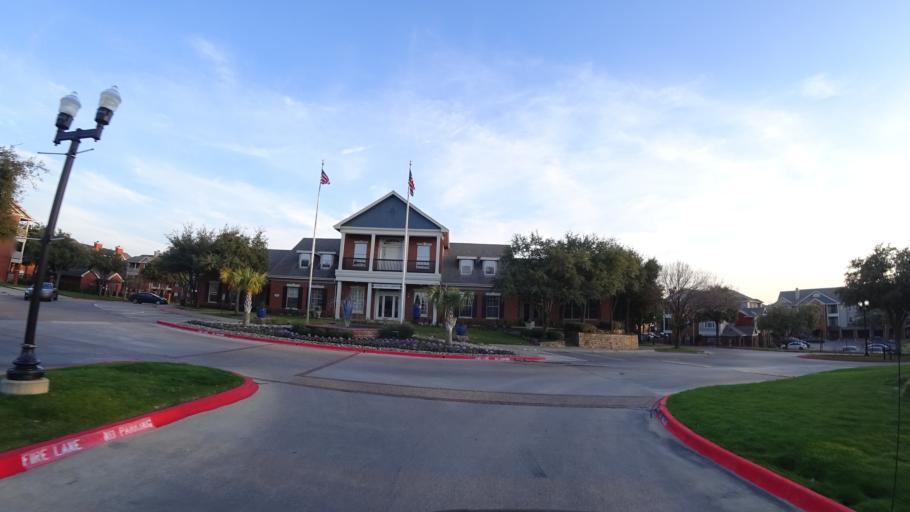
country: US
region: Texas
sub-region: Denton County
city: Lewisville
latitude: 33.0019
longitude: -96.9842
